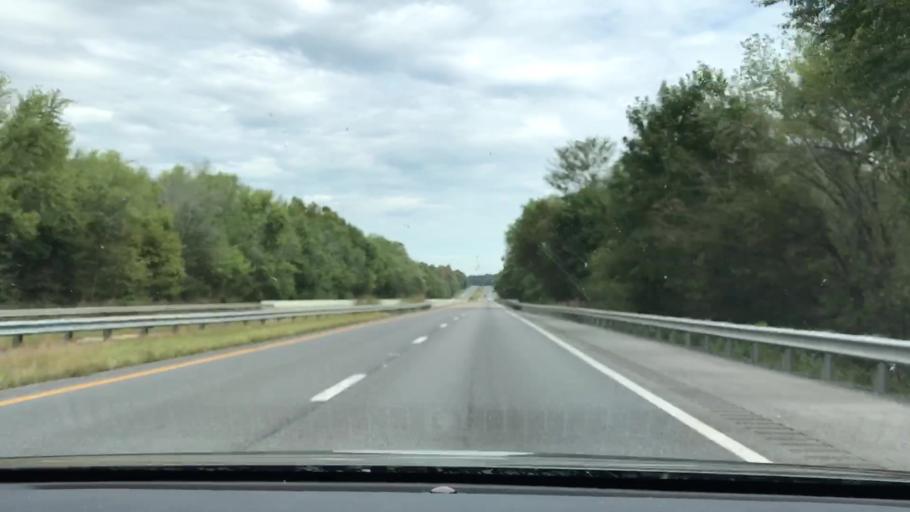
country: US
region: Kentucky
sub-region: Marshall County
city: Benton
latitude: 36.8819
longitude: -88.3570
